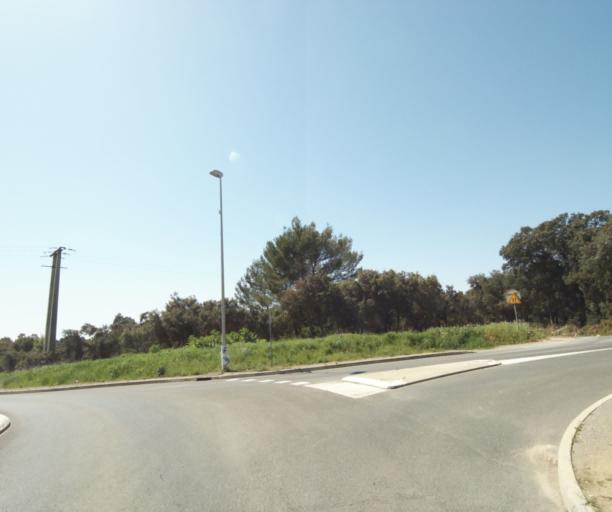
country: FR
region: Languedoc-Roussillon
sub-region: Departement de l'Herault
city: Castries
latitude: 43.6702
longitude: 3.9914
